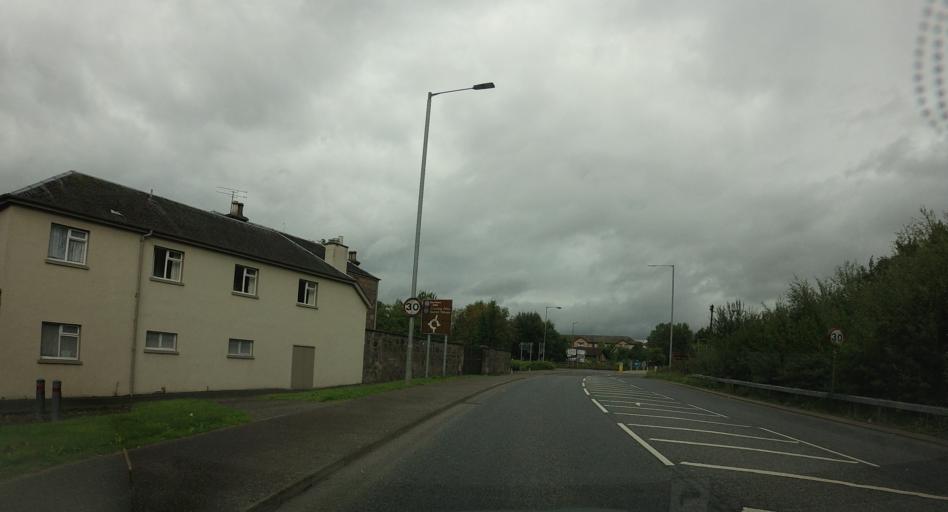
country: GB
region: Scotland
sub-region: Clackmannanshire
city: Alloa
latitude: 56.1204
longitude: -3.7794
